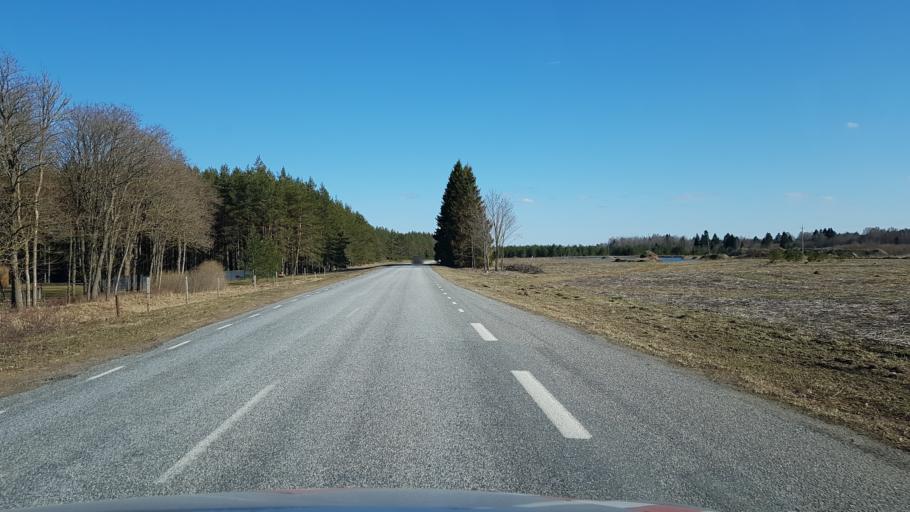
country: EE
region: Laeaene-Virumaa
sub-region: Haljala vald
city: Haljala
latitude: 59.4705
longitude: 26.1747
